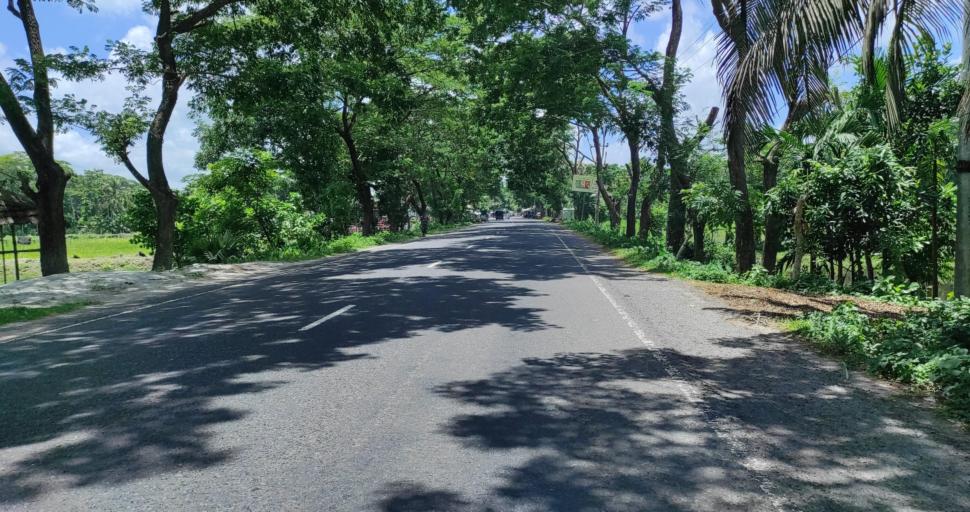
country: BD
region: Barisal
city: Barisal
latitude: 22.8192
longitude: 90.2709
